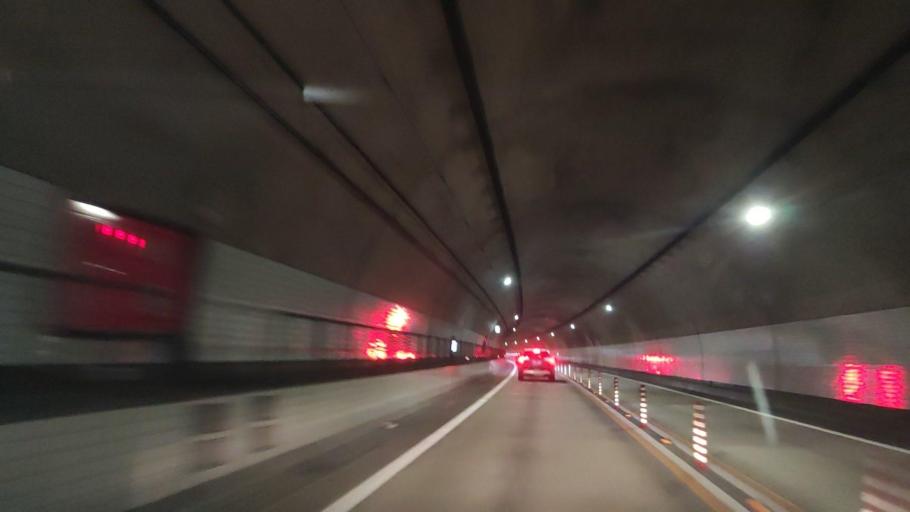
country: JP
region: Kyoto
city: Miyazu
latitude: 35.5587
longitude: 135.1239
